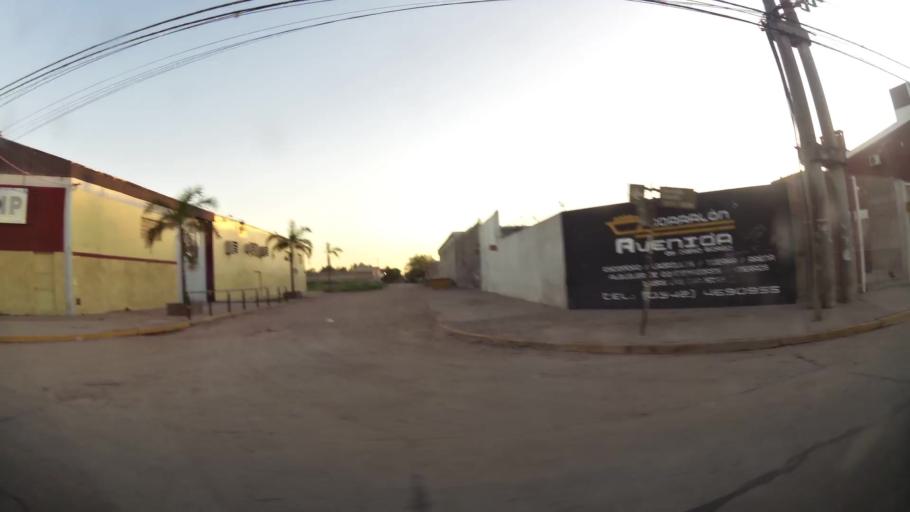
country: AR
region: Santa Fe
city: Santa Fe de la Vera Cruz
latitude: -31.5897
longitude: -60.6969
